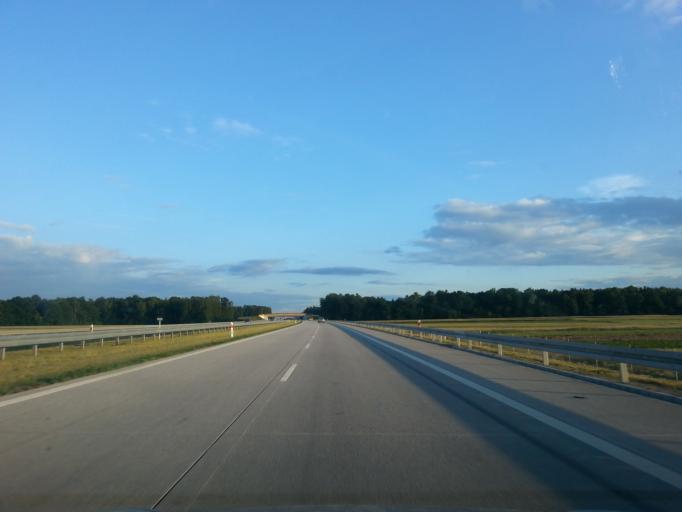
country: PL
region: Lodz Voivodeship
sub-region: Powiat sieradzki
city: Zloczew
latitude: 51.4465
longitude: 18.6459
